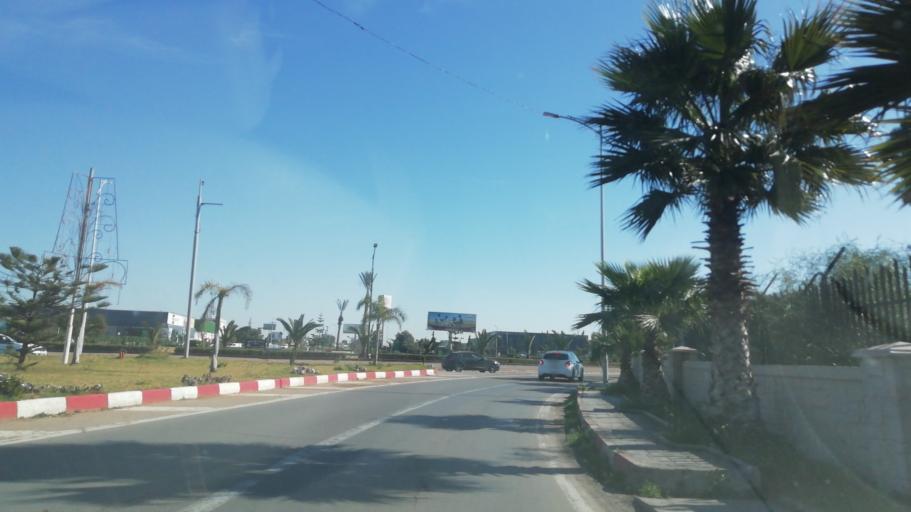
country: DZ
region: Oran
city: Es Senia
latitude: 35.6223
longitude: -0.5936
